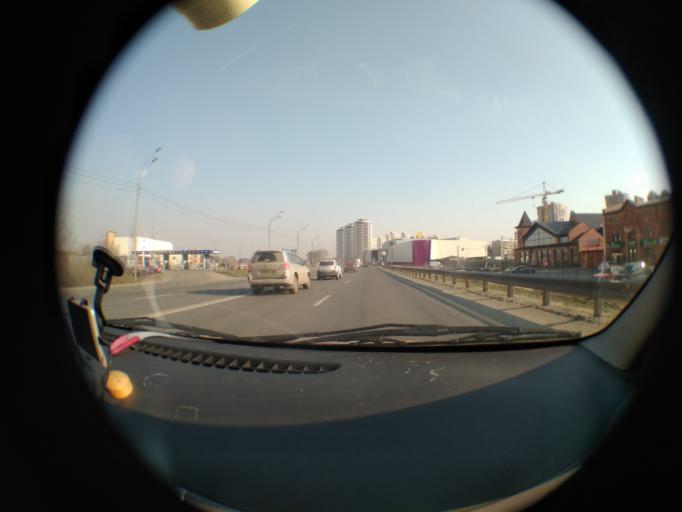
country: RU
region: Moskovskaya
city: Oktyabr'skiy
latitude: 55.6023
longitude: 37.9813
